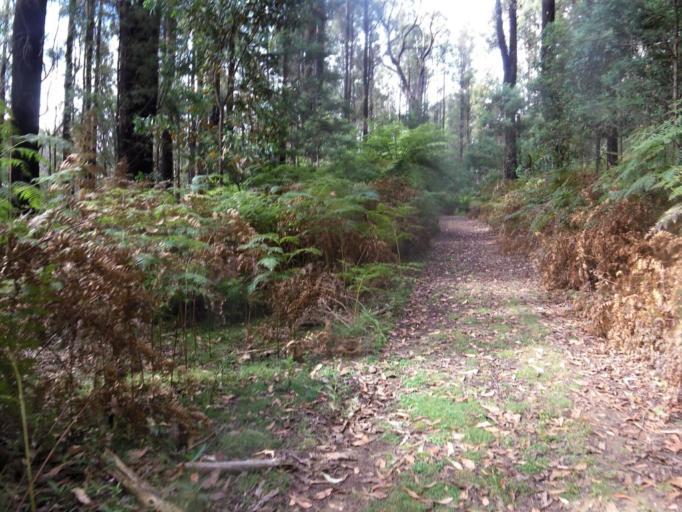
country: AU
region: Victoria
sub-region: Murrindindi
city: Alexandra
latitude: -37.3953
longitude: 145.5810
